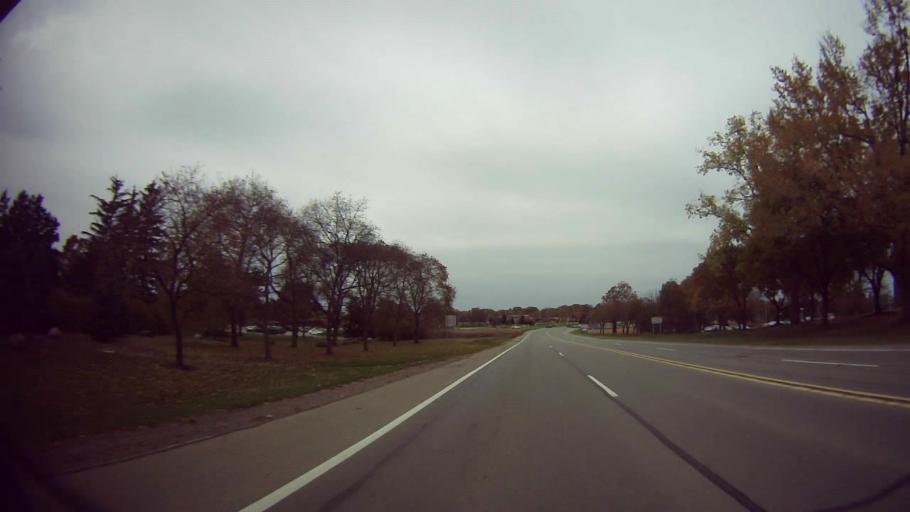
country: US
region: Michigan
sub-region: Oakland County
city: Pontiac
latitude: 42.6566
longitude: -83.3319
